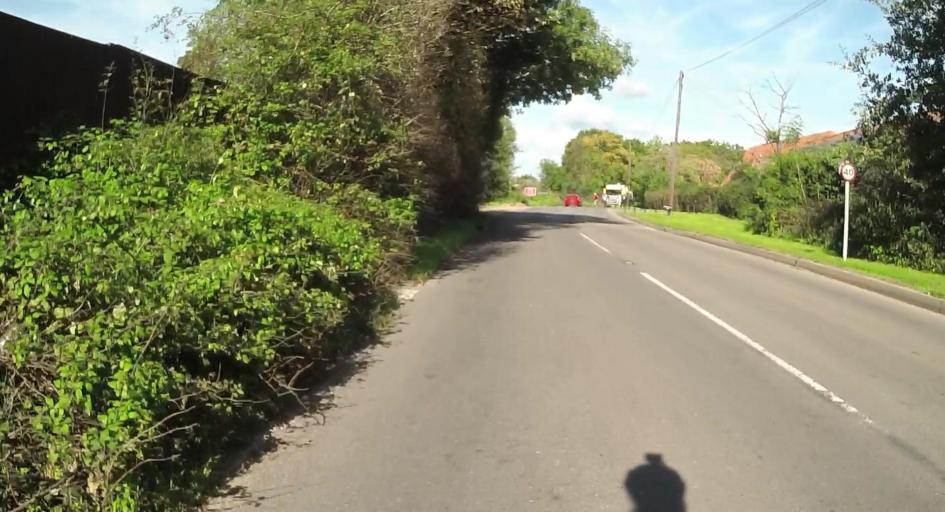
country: GB
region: England
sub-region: Surrey
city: Chertsey
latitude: 51.3821
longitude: -0.5245
